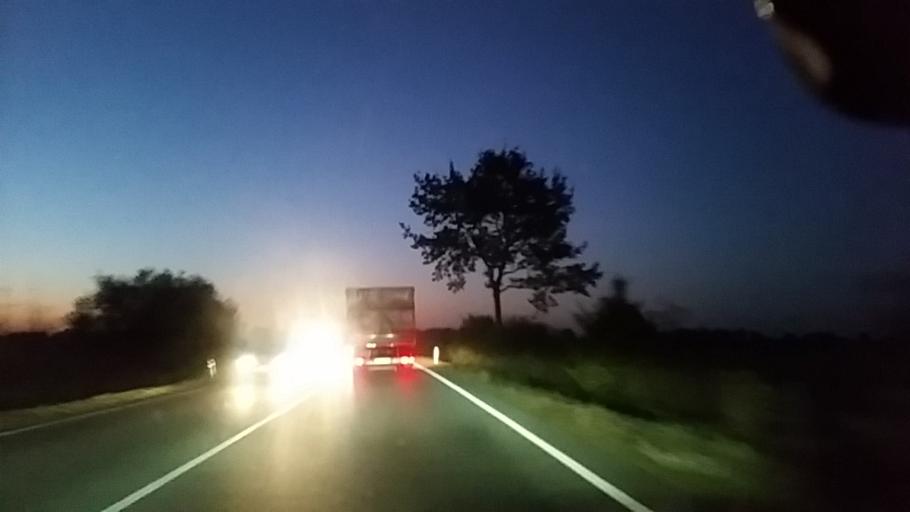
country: DE
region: Lower Saxony
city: Handorf
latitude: 53.3925
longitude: 10.3346
